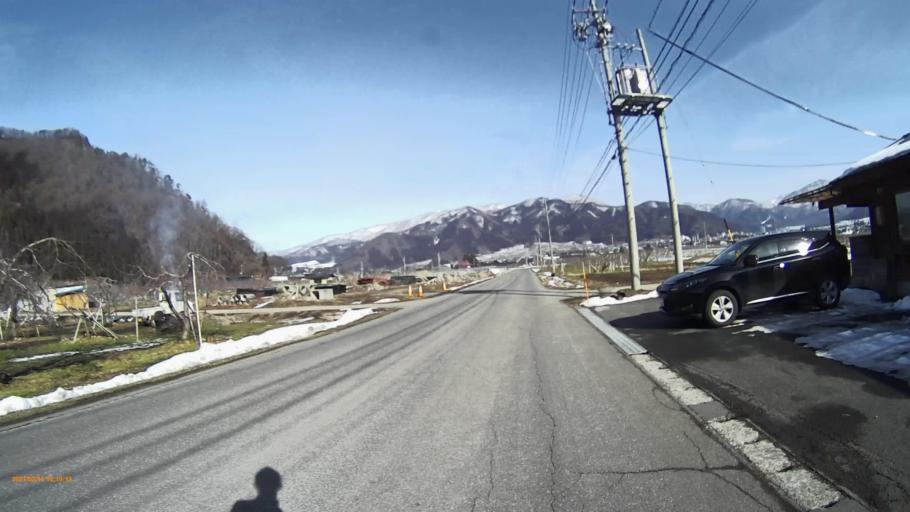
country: JP
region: Nagano
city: Nakano
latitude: 36.7465
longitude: 138.3900
